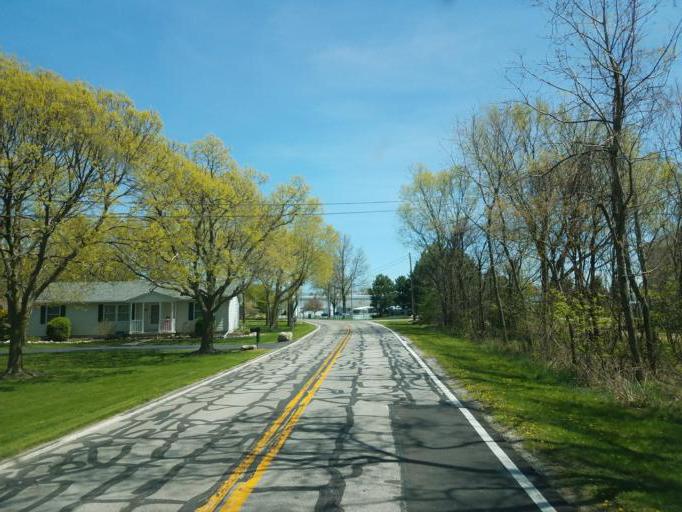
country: US
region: Ohio
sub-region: Ottawa County
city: Port Clinton
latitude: 41.5718
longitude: -82.8293
